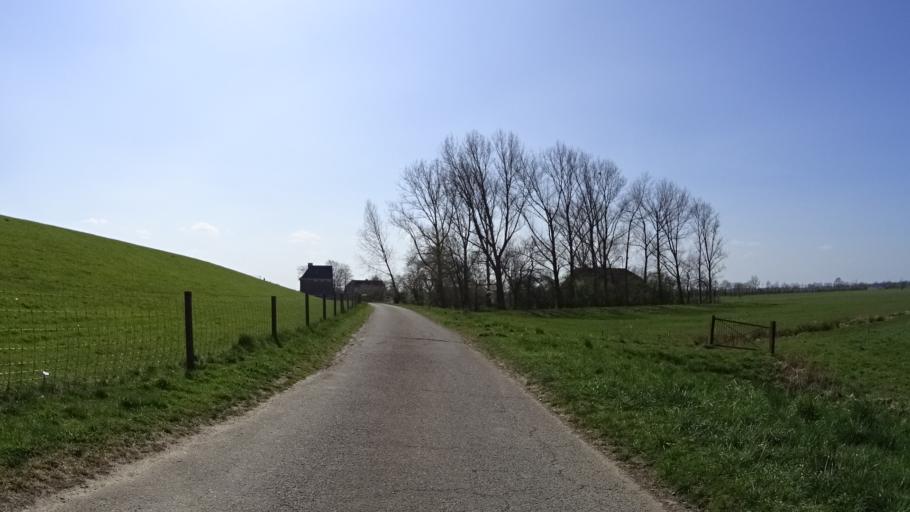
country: DE
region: Lower Saxony
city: Weener
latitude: 53.1350
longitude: 7.3632
